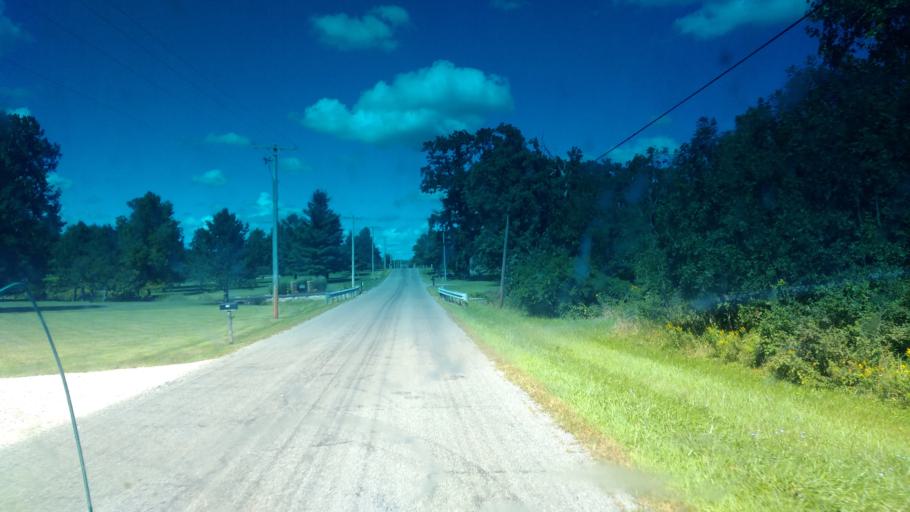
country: US
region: Ohio
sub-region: Madison County
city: Choctaw Lake
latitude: 40.0158
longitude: -83.3901
